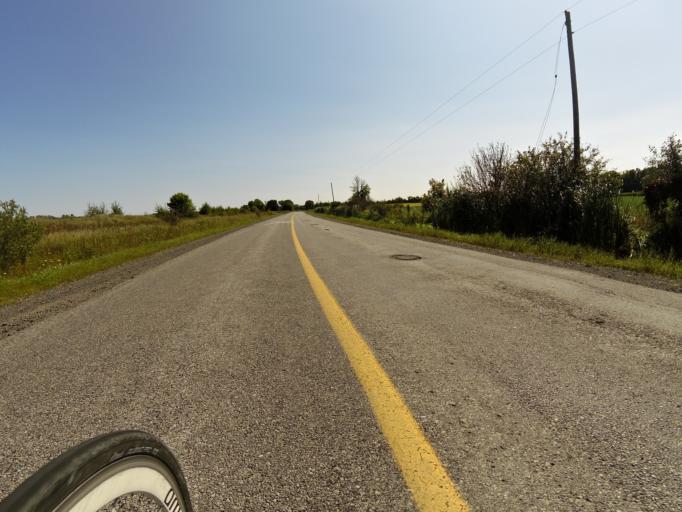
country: CA
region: Ontario
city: Arnprior
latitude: 45.4470
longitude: -76.0796
